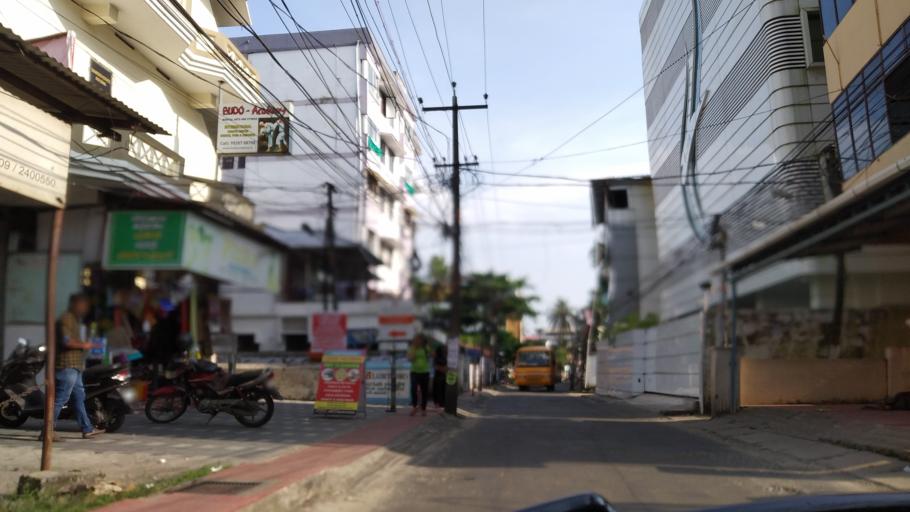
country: IN
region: Kerala
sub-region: Ernakulam
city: Cochin
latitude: 9.9971
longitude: 76.2860
